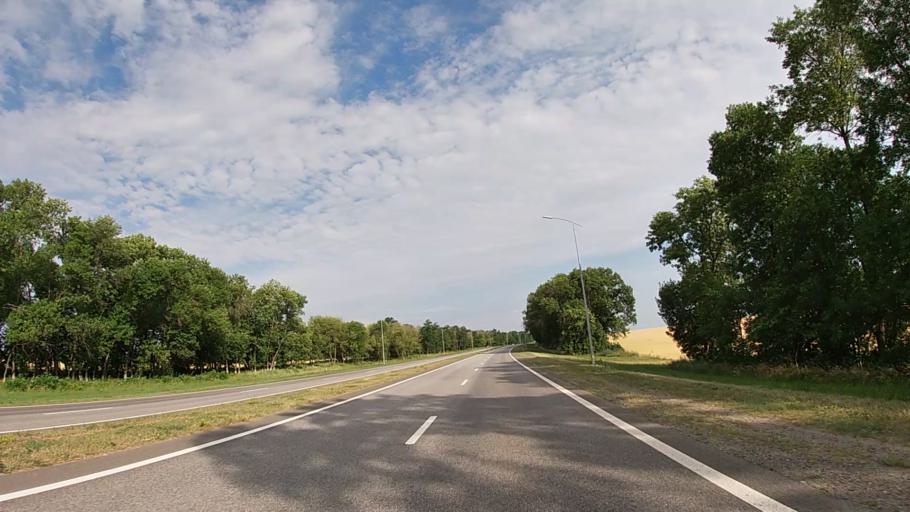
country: RU
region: Belgorod
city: Tomarovka
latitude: 50.6720
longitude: 36.2997
